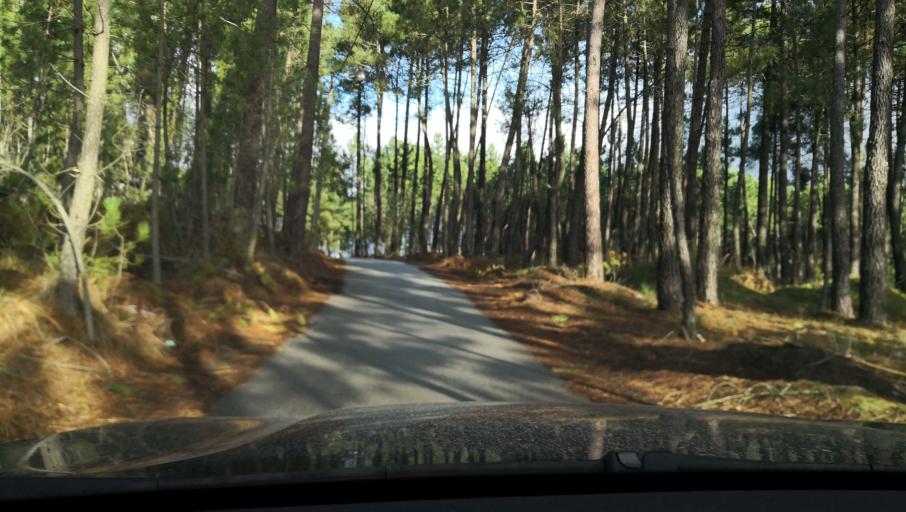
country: PT
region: Vila Real
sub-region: Vila Real
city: Vila Real
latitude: 41.2730
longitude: -7.7158
